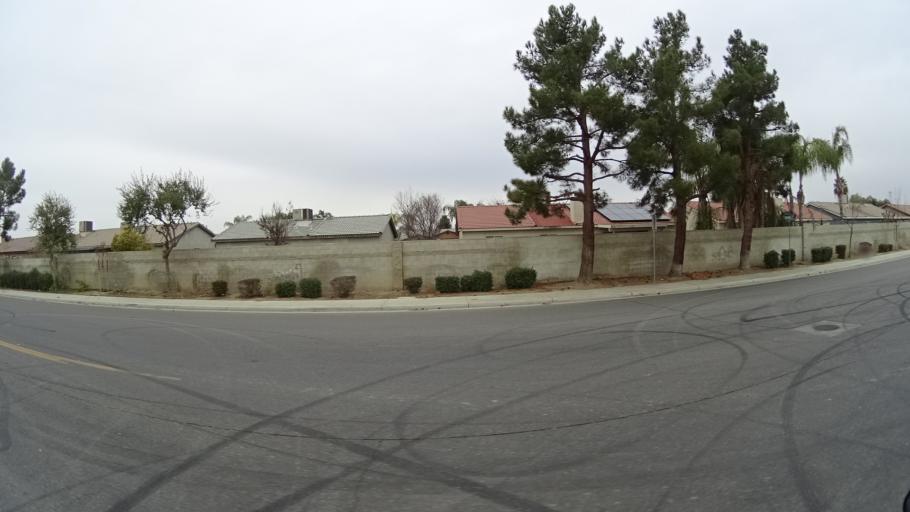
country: US
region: California
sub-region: Kern County
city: Bakersfield
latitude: 35.3469
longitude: -118.9473
